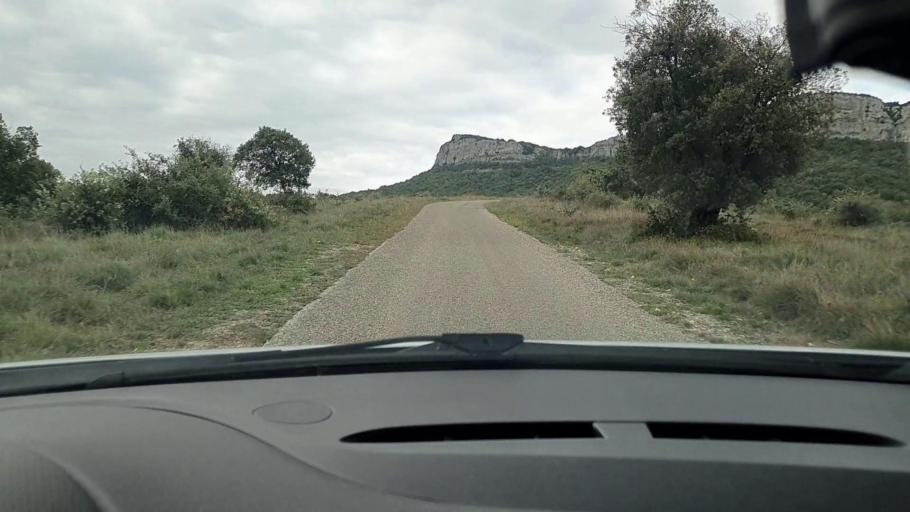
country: FR
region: Languedoc-Roussillon
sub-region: Departement du Gard
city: Mons
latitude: 44.1511
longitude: 4.2918
